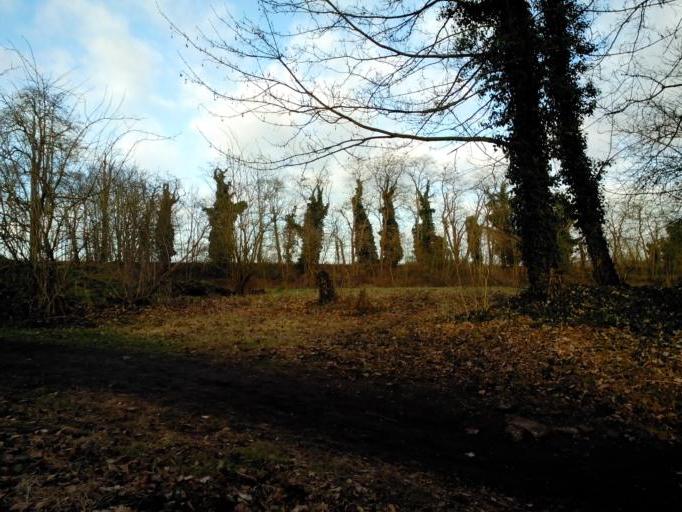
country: BE
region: Flanders
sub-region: Provincie Vlaams-Brabant
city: Leuven
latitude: 50.8647
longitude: 4.7193
